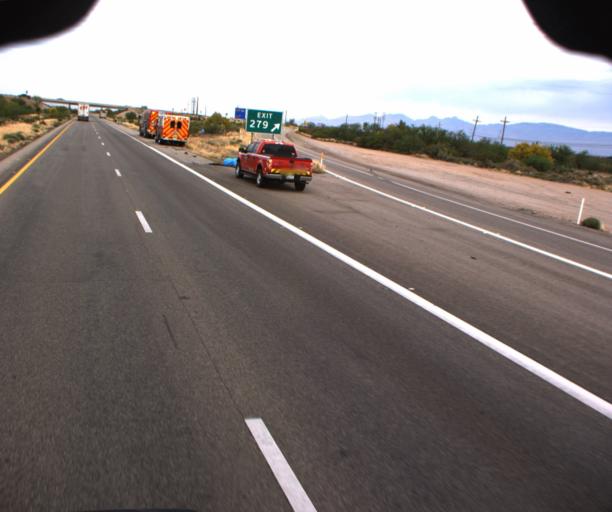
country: US
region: Arizona
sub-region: Pima County
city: Vail
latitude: 32.0264
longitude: -110.7177
